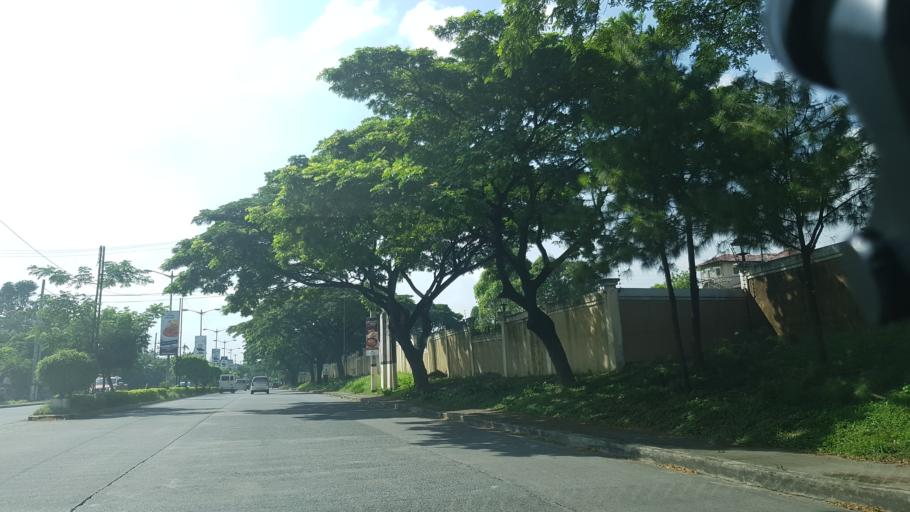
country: PH
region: Calabarzon
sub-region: Province of Laguna
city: San Pedro
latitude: 14.3829
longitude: 121.0116
